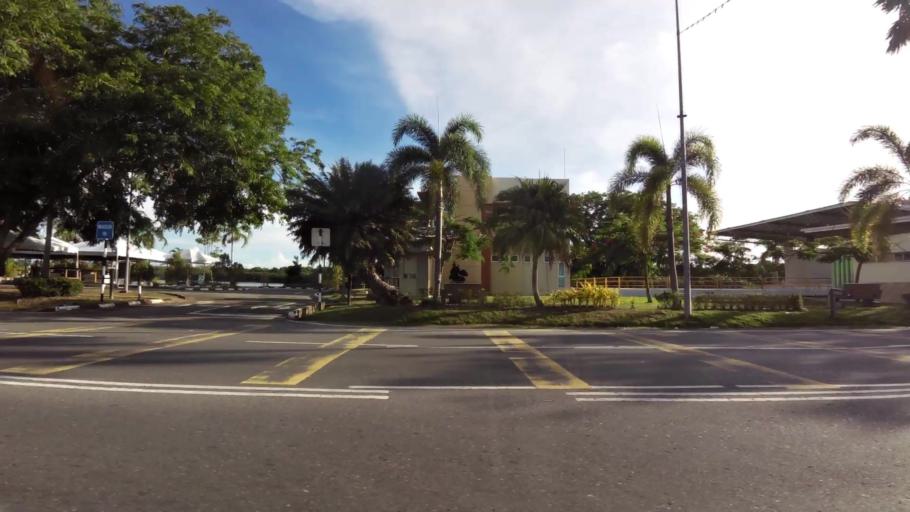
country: BN
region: Belait
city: Kuala Belait
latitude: 4.5809
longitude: 114.1930
